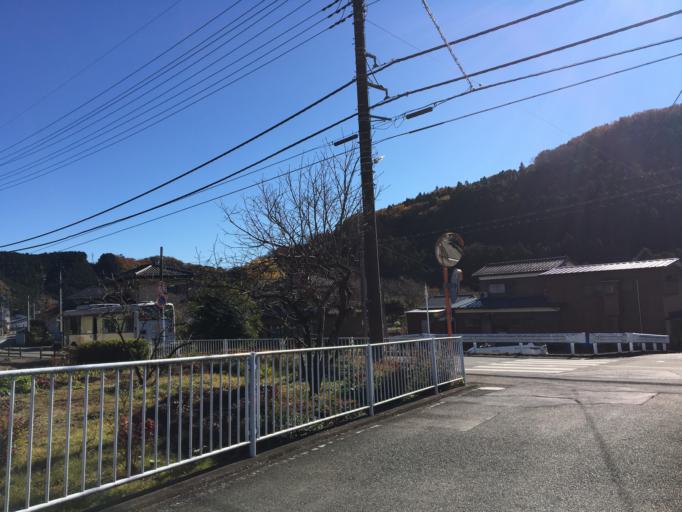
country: JP
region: Saitama
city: Ogawa
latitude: 36.0501
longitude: 139.2211
